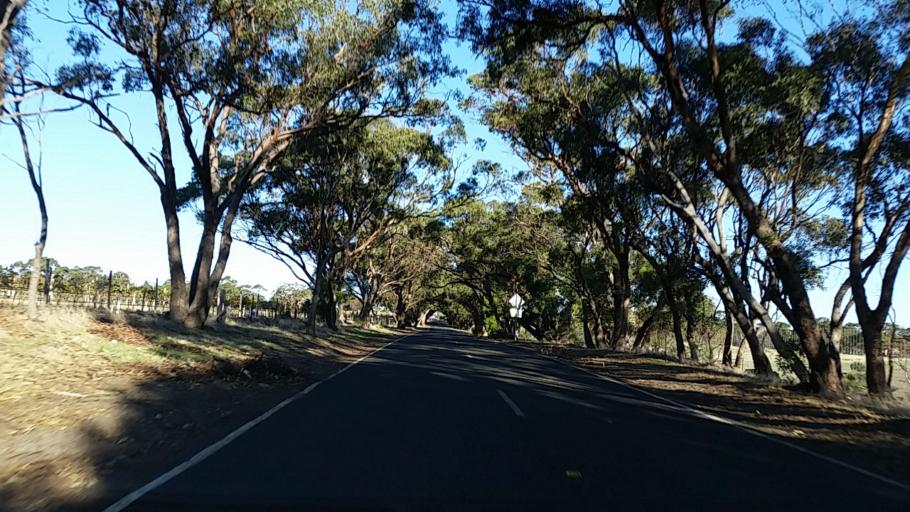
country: AU
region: South Australia
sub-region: Onkaparinga
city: Hackham
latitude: -35.1536
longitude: 138.5424
